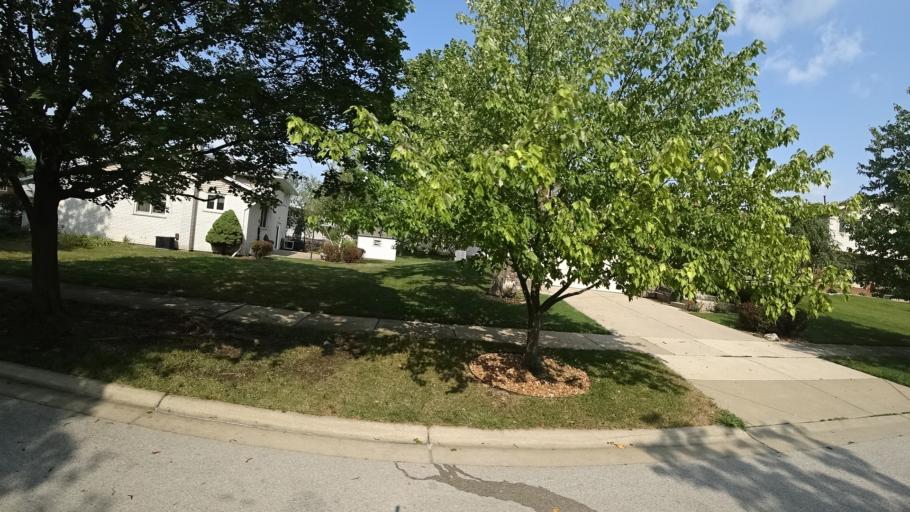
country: US
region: Illinois
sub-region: Cook County
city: Oak Forest
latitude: 41.6119
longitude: -87.7790
